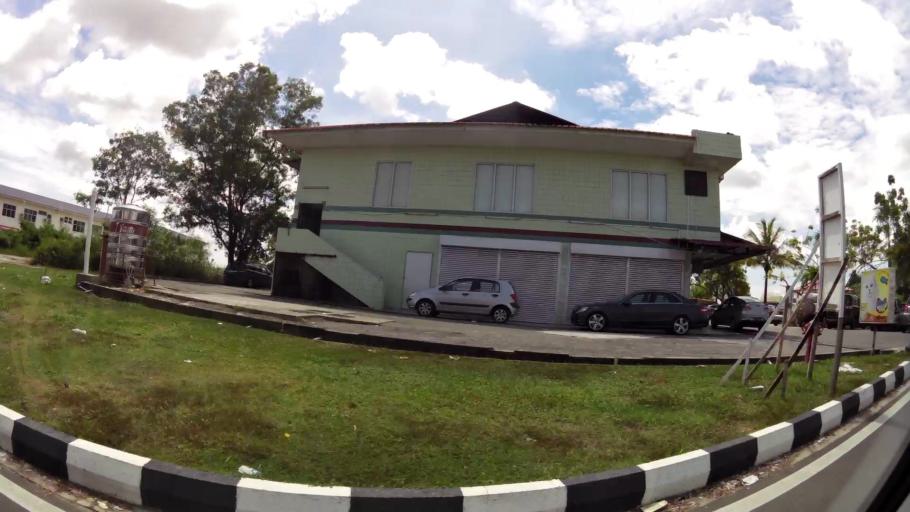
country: BN
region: Brunei and Muara
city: Bandar Seri Begawan
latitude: 4.9417
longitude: 114.9062
